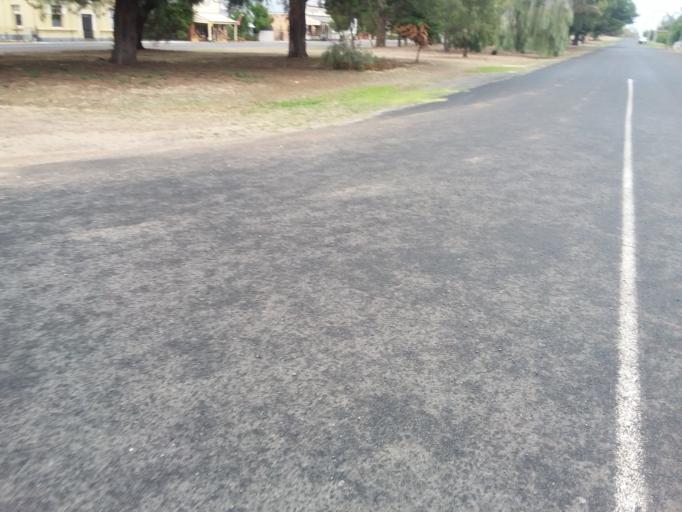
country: AU
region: Victoria
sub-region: Horsham
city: Horsham
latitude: -36.7418
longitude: 141.9411
